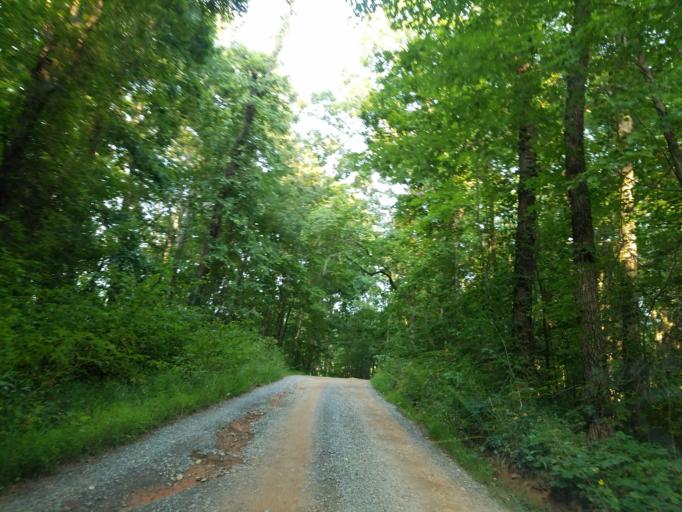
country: US
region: Georgia
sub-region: Gilmer County
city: Ellijay
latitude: 34.6558
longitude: -84.4445
